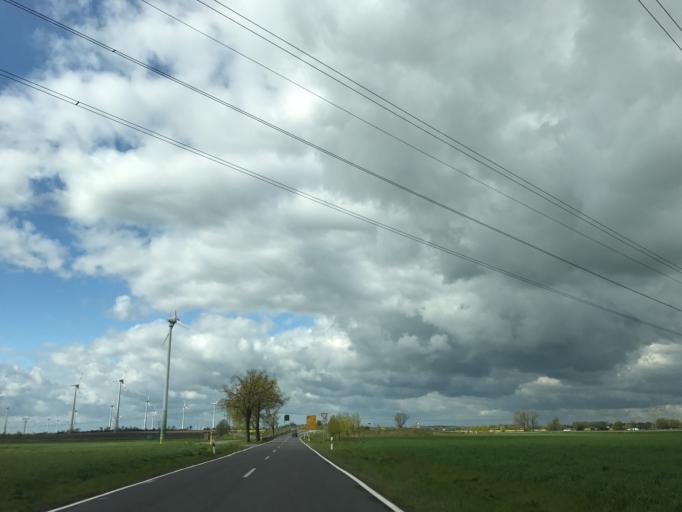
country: DE
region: Brandenburg
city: Nauen
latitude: 52.5804
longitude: 12.9116
